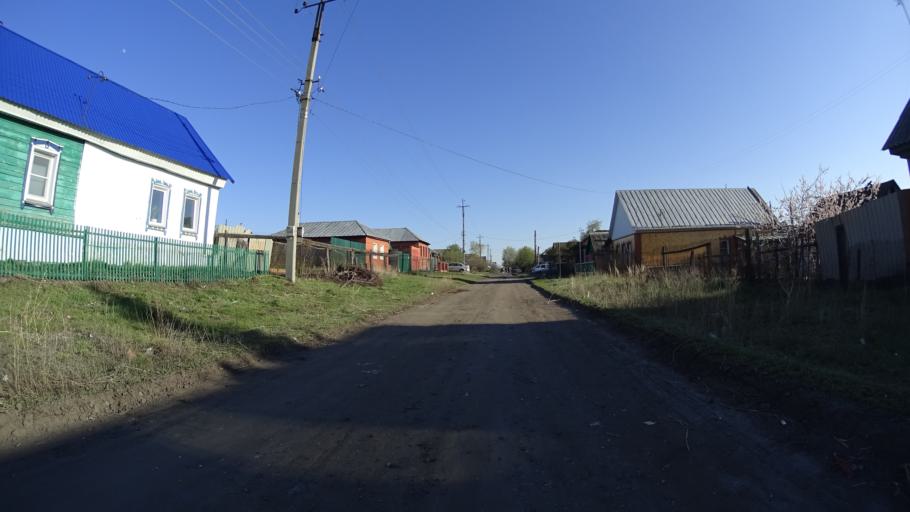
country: RU
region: Chelyabinsk
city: Troitsk
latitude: 54.0856
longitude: 61.5956
